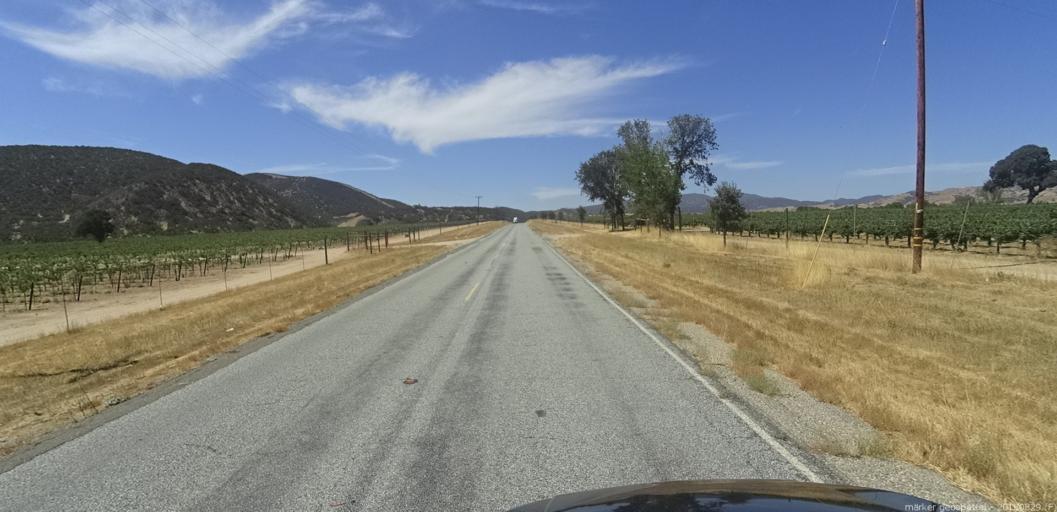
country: US
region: California
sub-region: San Luis Obispo County
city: Lake Nacimiento
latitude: 35.8831
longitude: -120.9085
